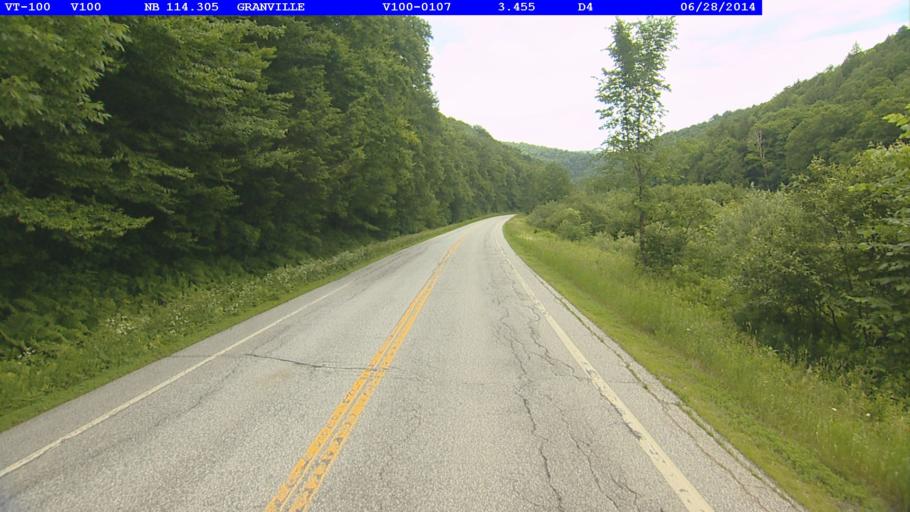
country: US
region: Vermont
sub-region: Orange County
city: Randolph
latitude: 43.9912
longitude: -72.8524
